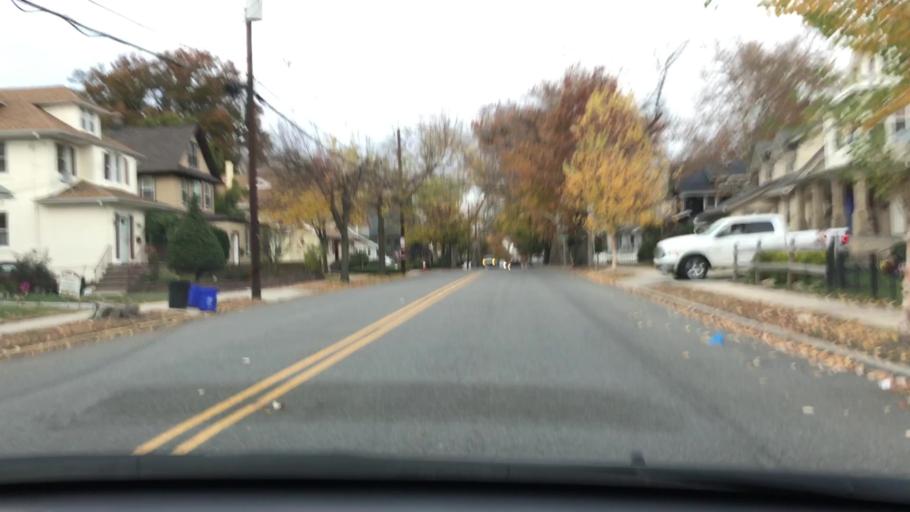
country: US
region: New Jersey
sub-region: Bergen County
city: Bogota
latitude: 40.8713
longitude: -74.0276
